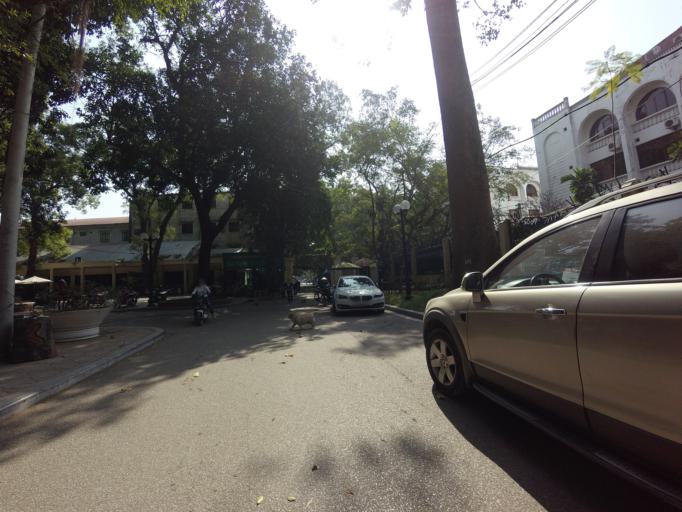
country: VN
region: Ha Noi
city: Hanoi
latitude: 21.0389
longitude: 105.8310
